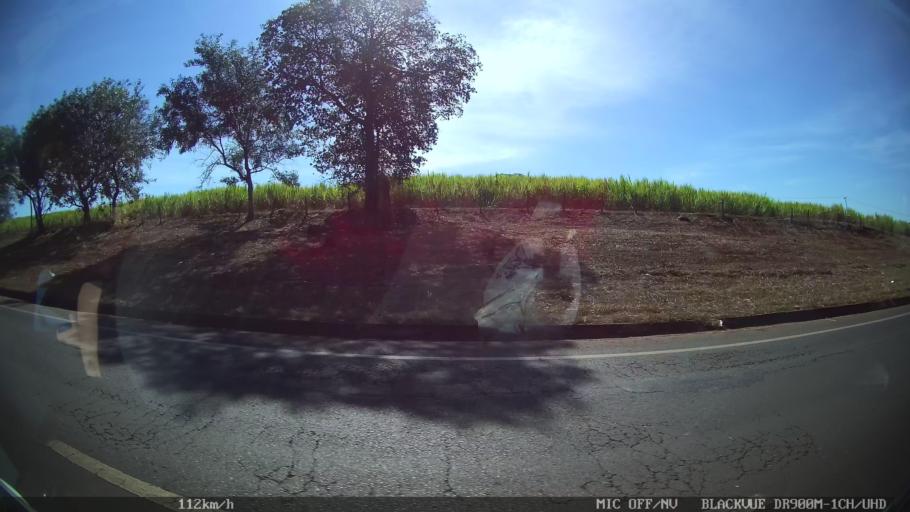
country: BR
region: Sao Paulo
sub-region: Ipua
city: Ipua
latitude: -20.4932
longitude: -48.0230
